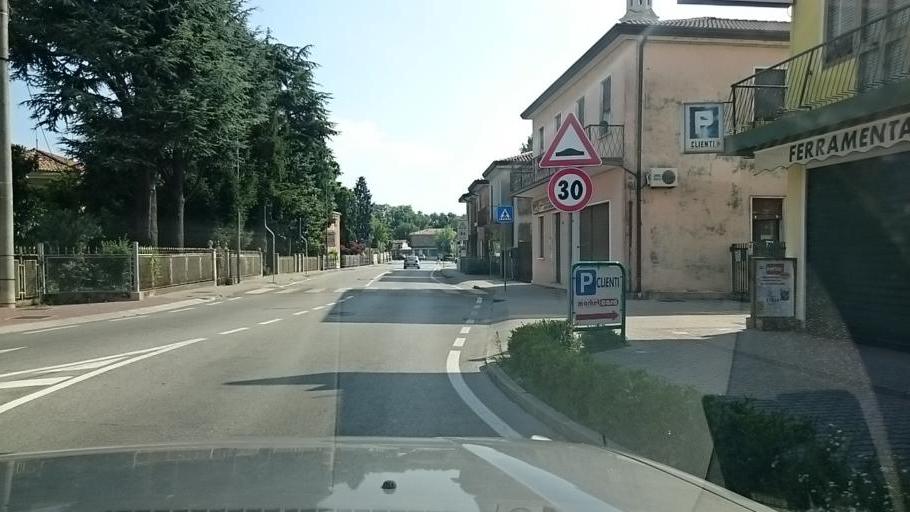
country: IT
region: Veneto
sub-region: Provincia di Padova
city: Vigodarzere
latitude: 45.4564
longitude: 11.8820
